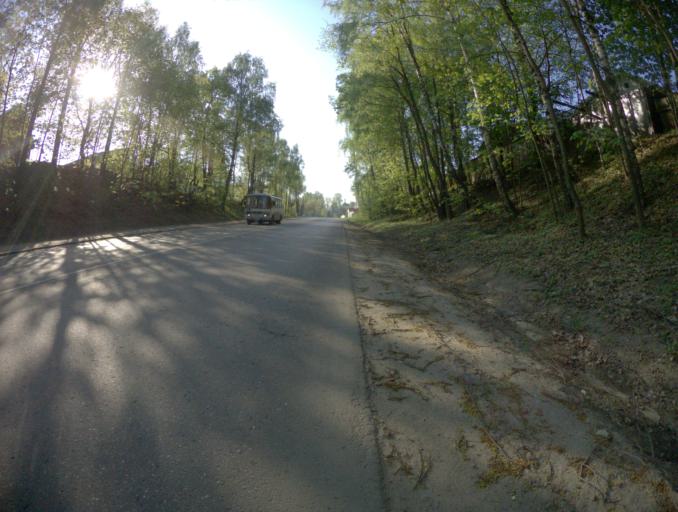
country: RU
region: Vladimir
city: Vyazniki
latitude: 56.2398
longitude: 42.1712
